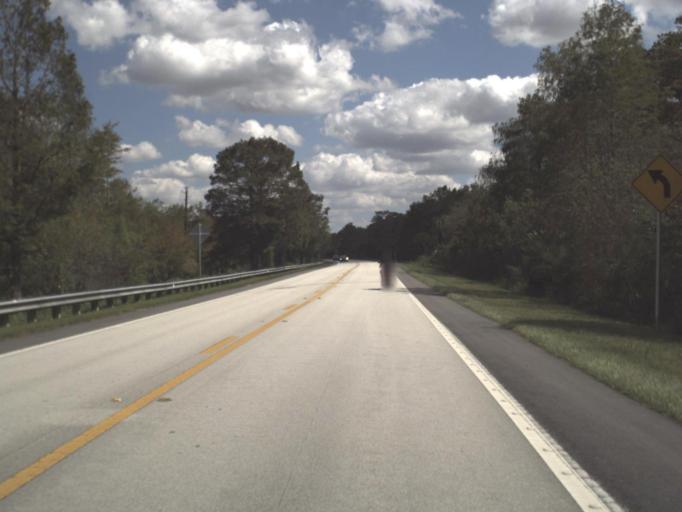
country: US
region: Florida
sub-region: Collier County
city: Marco
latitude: 25.8795
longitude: -81.2434
